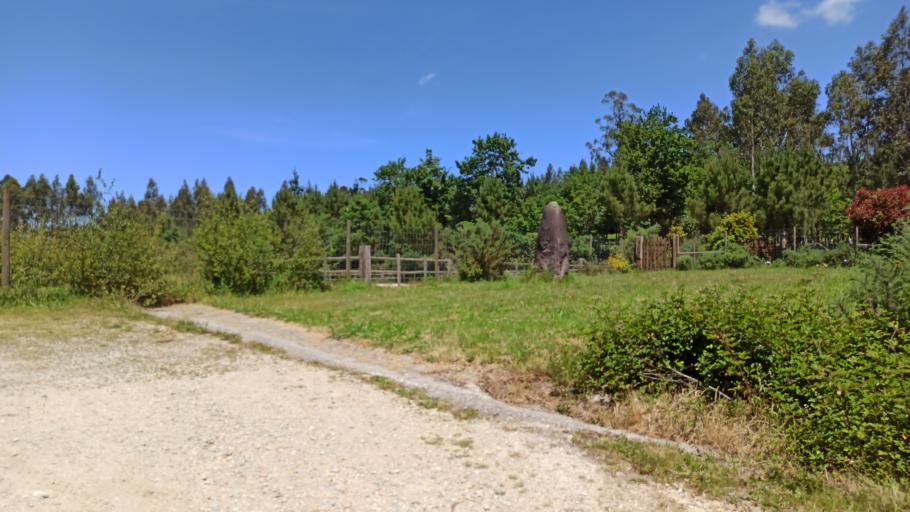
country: ES
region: Galicia
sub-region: Provincia da Coruna
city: Negreira
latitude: 42.9167
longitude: -8.7209
